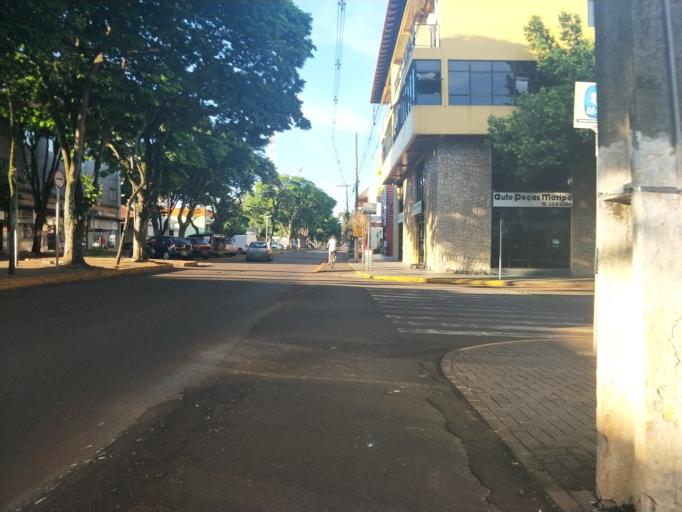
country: BR
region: Parana
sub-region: Marechal Candido Rondon
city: Marechal Candido Rondon
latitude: -24.5623
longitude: -54.0585
